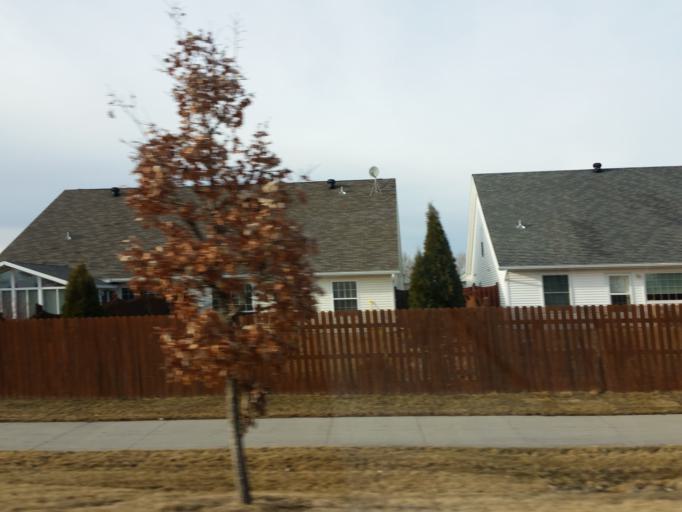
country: US
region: North Dakota
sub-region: Cass County
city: West Fargo
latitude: 46.8626
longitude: -96.9165
